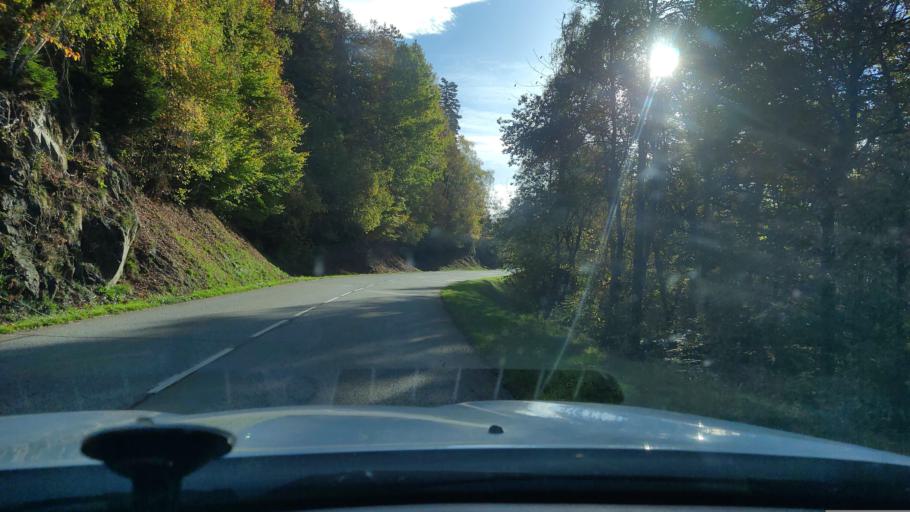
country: FR
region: Rhone-Alpes
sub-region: Departement de la Savoie
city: Beaufort
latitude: 45.7338
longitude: 6.5564
